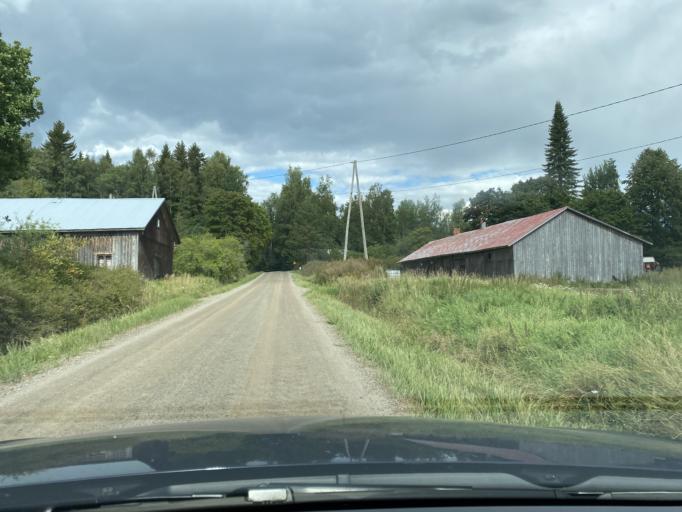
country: FI
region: Haeme
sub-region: Forssa
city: Humppila
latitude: 61.0744
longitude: 23.2738
